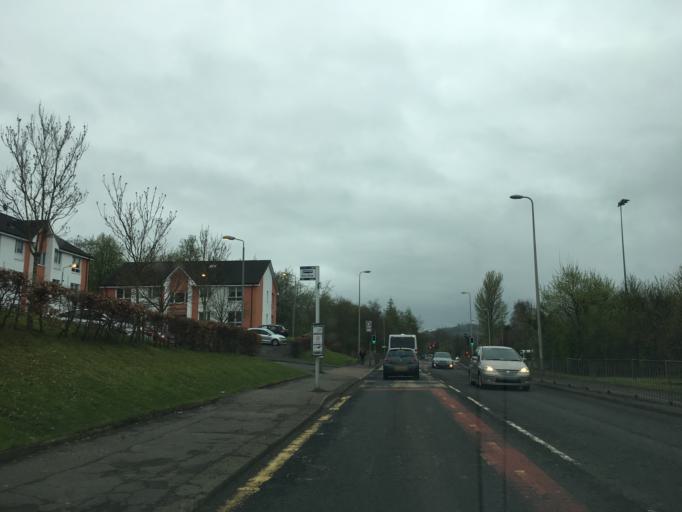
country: GB
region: Scotland
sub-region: Inverclyde
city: Gourock
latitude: 55.9381
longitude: -4.8113
